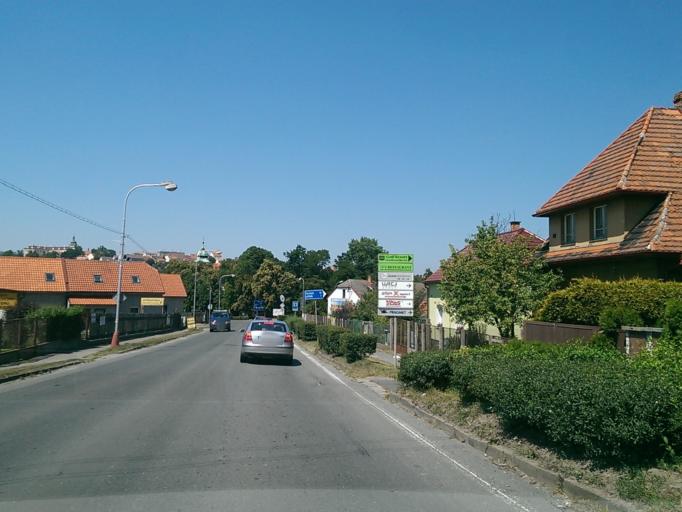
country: CZ
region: Central Bohemia
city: Benatky nad Jizerou
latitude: 50.2826
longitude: 14.8303
